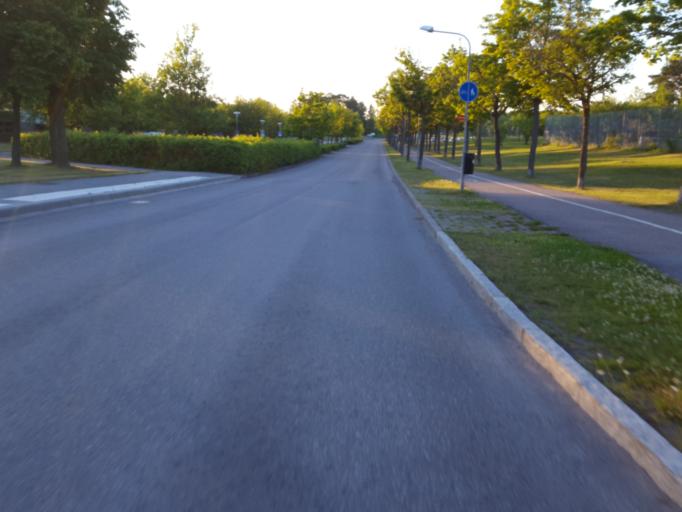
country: SE
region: Uppsala
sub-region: Uppsala Kommun
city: Saevja
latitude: 59.8193
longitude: 17.6573
